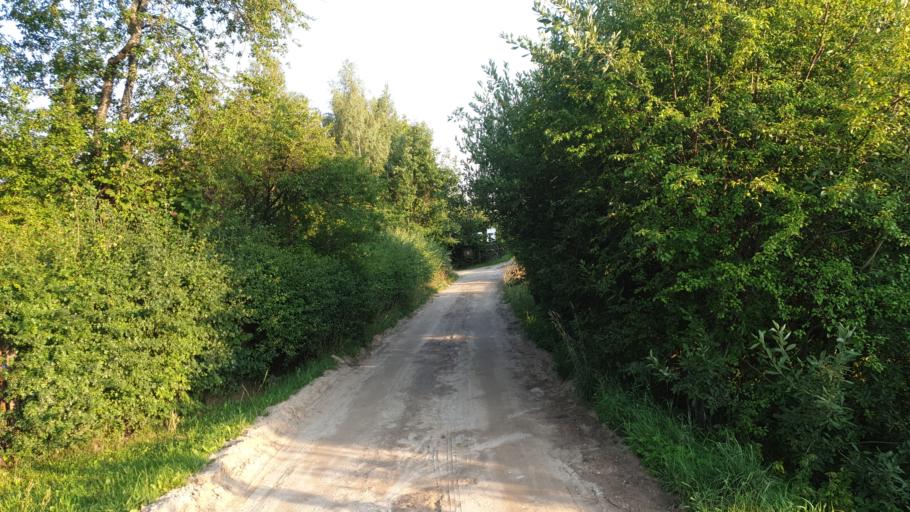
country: LT
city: Grigiskes
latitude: 54.7625
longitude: 25.0257
